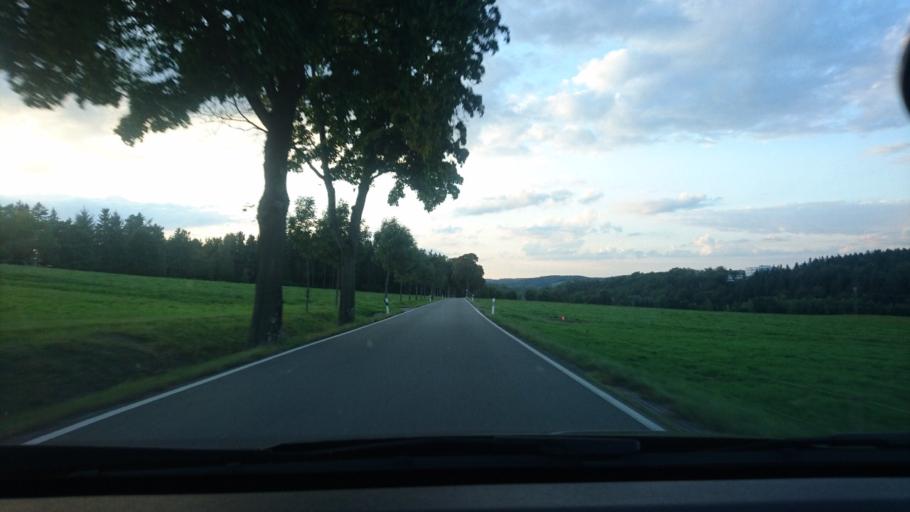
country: DE
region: Saxony
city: Auerbach
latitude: 50.5155
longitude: 12.4114
